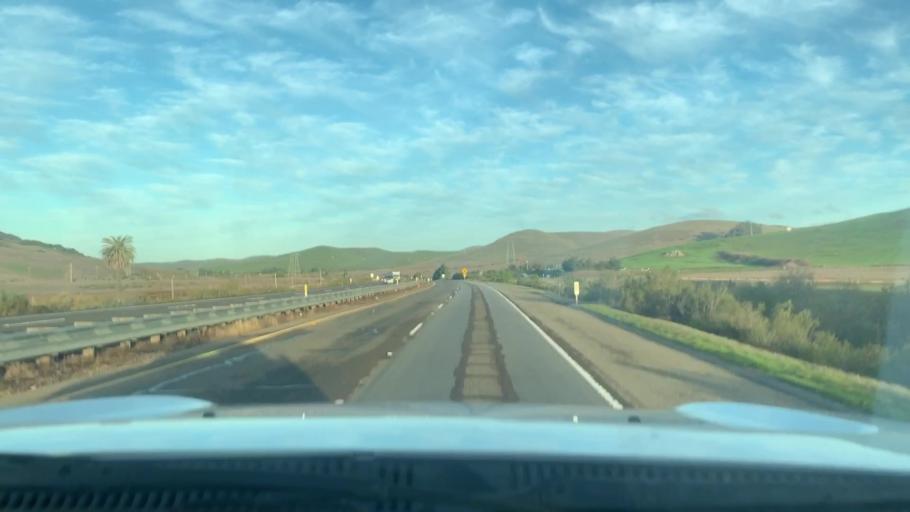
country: US
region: California
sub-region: San Luis Obispo County
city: Los Osos
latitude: 35.3420
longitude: -120.7635
